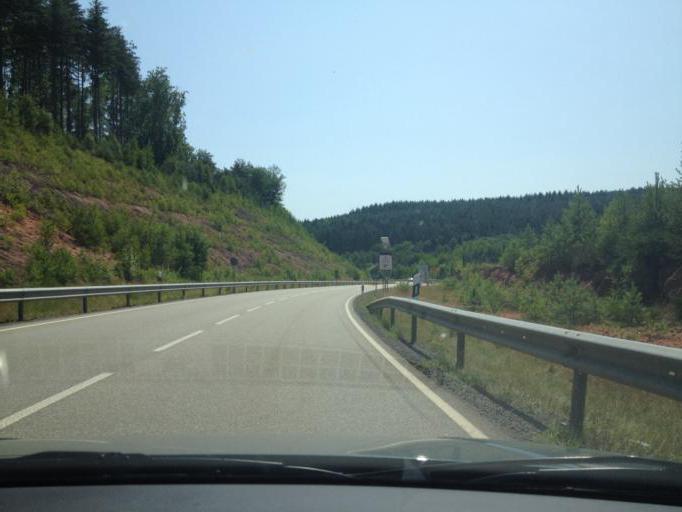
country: DE
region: Rheinland-Pfalz
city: Fischbach
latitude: 49.4461
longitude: 7.9143
